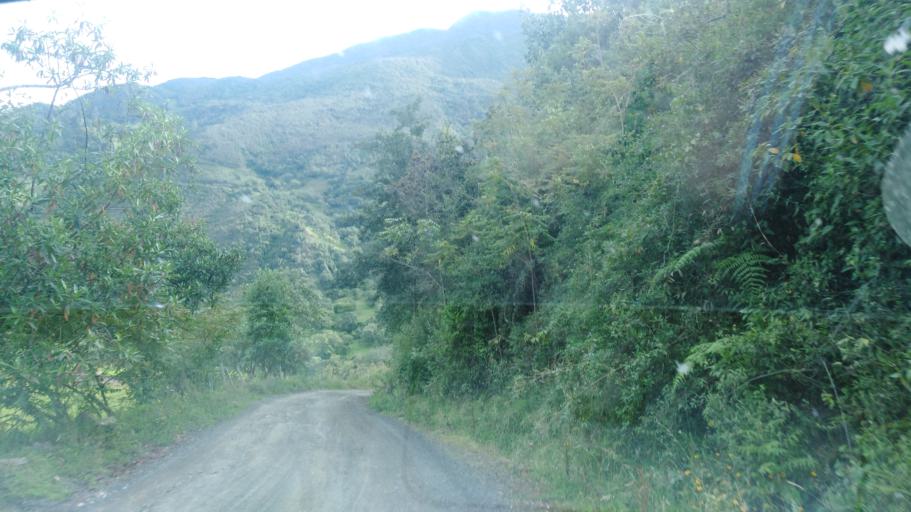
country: CO
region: Boyaca
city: San Mateo
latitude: 6.4202
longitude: -72.5633
